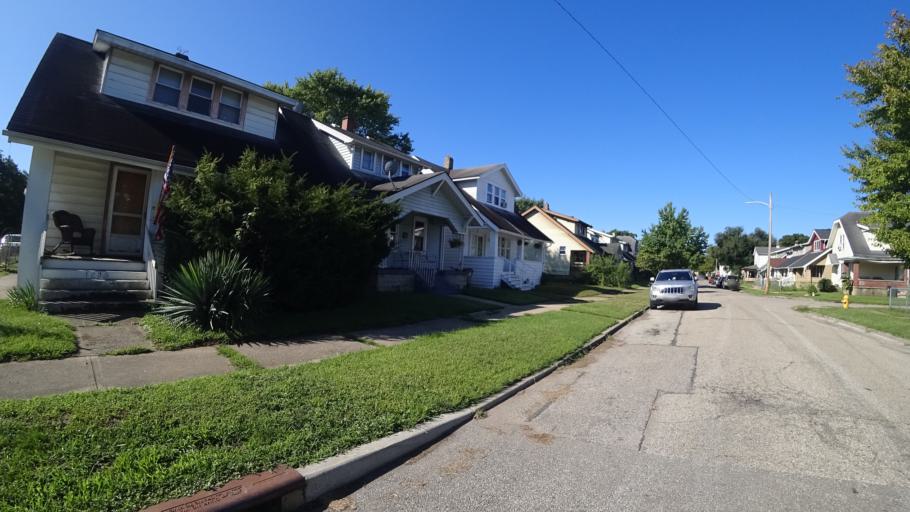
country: US
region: Ohio
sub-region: Butler County
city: Hamilton
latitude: 39.4066
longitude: -84.5446
